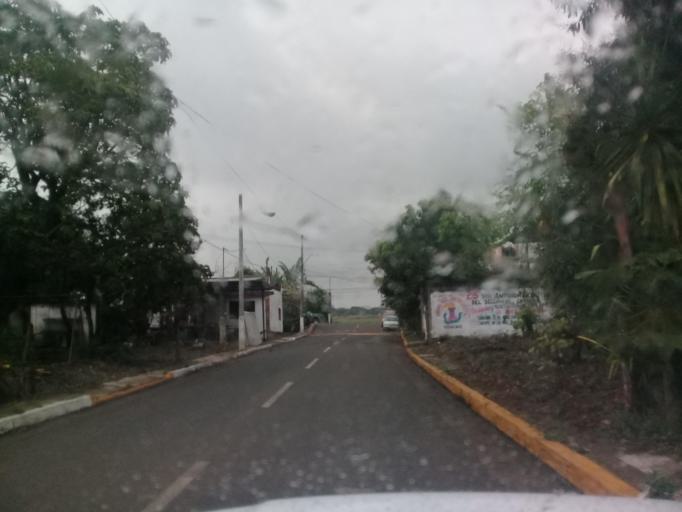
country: MX
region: Veracruz
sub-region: Cordoba
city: Veinte de Noviembre
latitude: 18.8677
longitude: -96.9538
